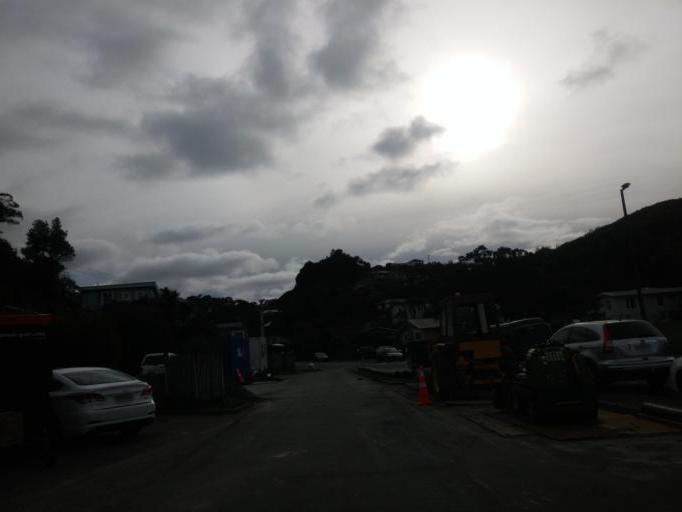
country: NZ
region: Wellington
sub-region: Wellington City
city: Brooklyn
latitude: -41.3170
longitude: 174.7698
